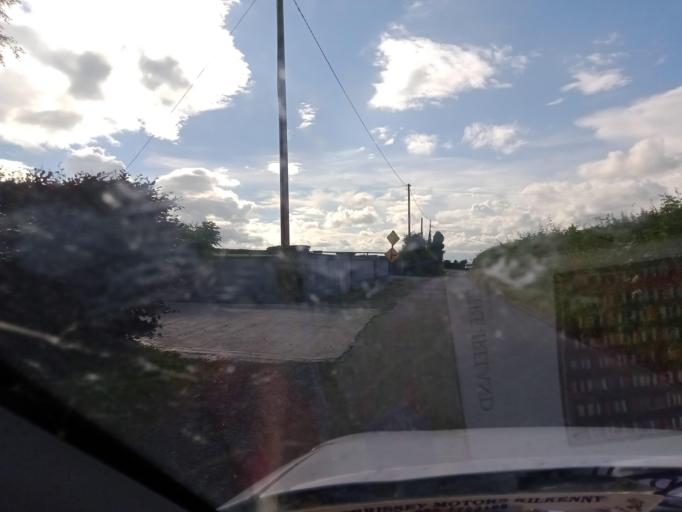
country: IE
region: Leinster
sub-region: Laois
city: Rathdowney
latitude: 52.7722
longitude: -7.5002
